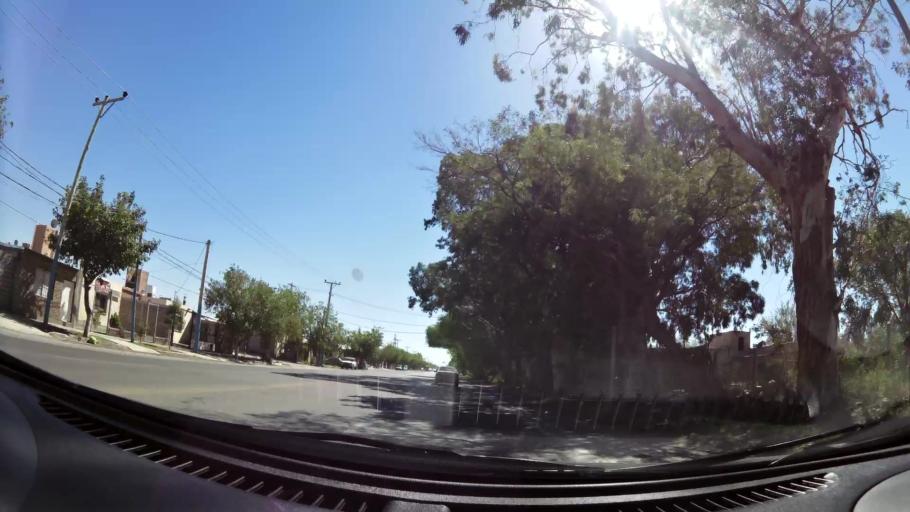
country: AR
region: San Juan
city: Villa Krause
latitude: -31.5965
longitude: -68.5402
